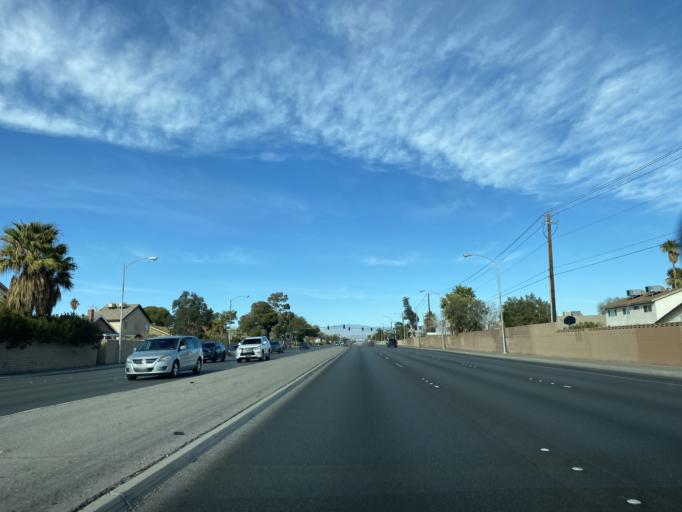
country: US
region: Nevada
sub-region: Clark County
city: Spring Valley
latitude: 36.1203
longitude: -115.2429
